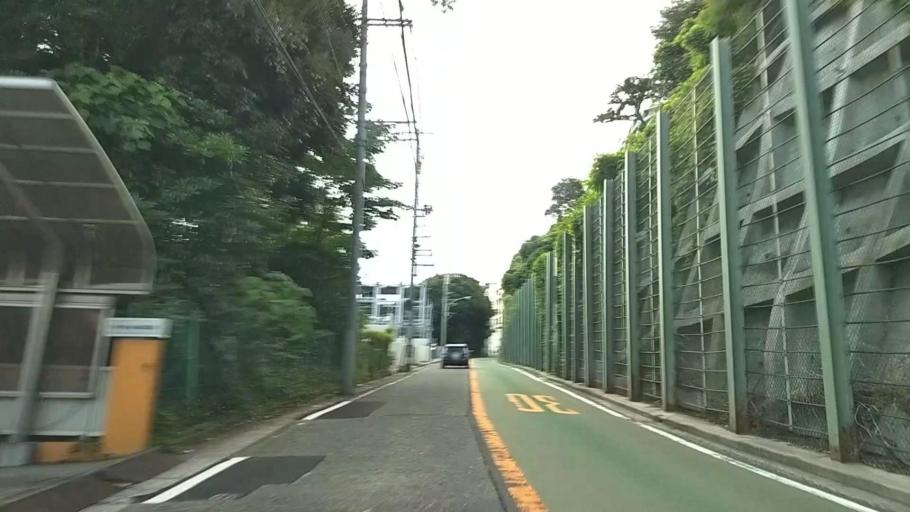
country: JP
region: Kanagawa
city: Yokohama
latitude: 35.4192
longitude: 139.6396
